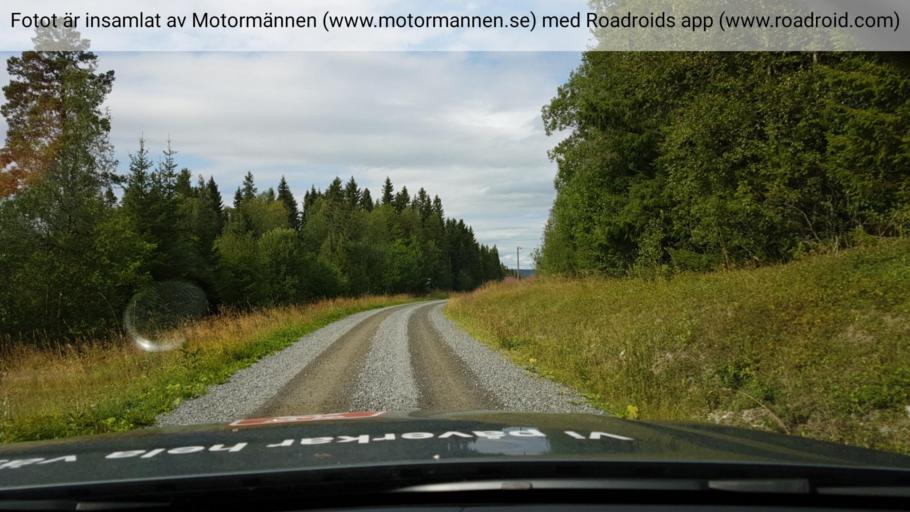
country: SE
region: Jaemtland
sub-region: Krokoms Kommun
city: Valla
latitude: 63.5280
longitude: 13.8820
